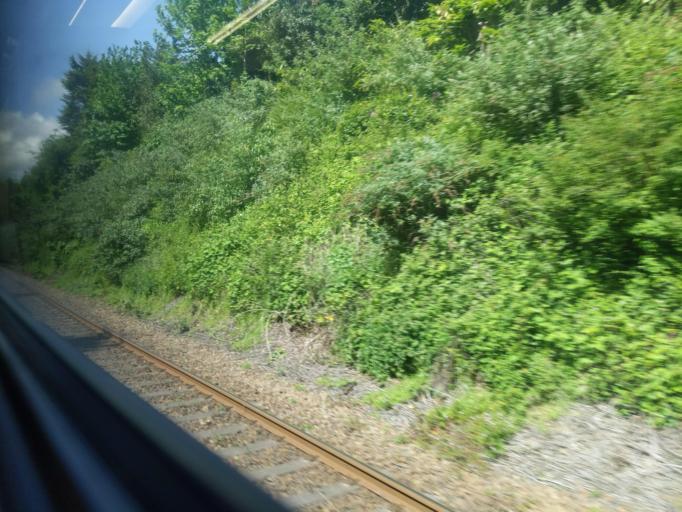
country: GB
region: England
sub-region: Cornwall
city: St Austell
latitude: 50.3413
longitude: -4.7954
